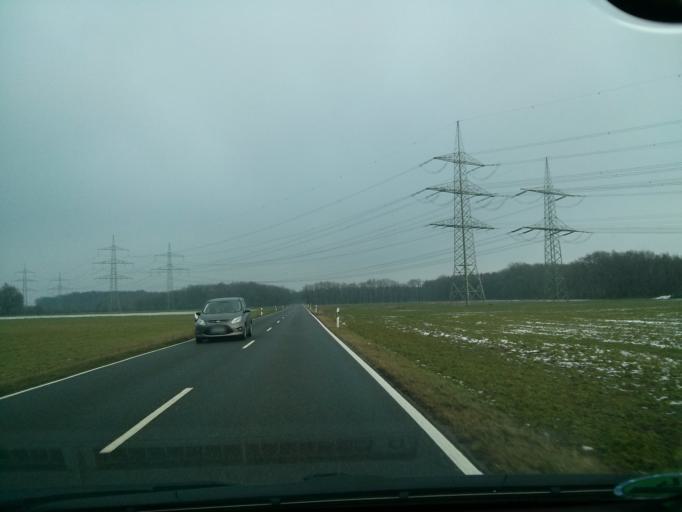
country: DE
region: North Rhine-Westphalia
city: Meckenheim
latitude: 50.6613
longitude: 7.0068
